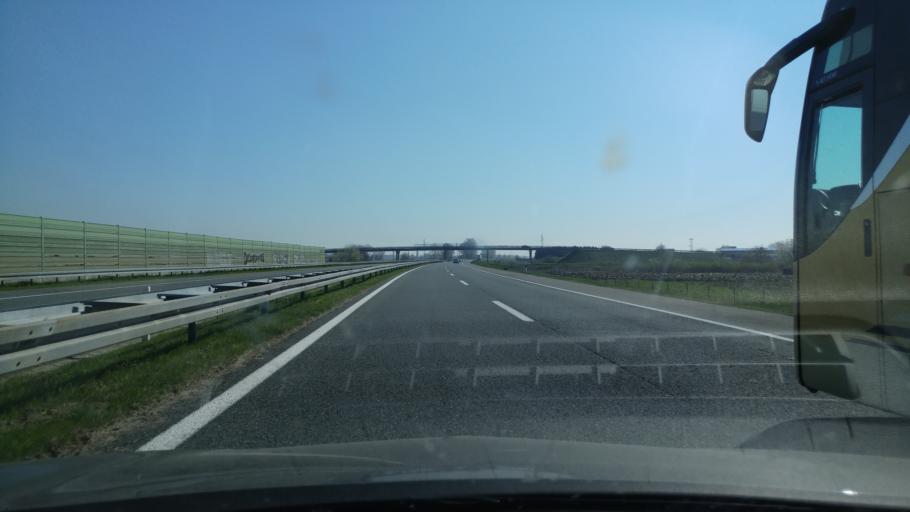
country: HR
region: Brodsko-Posavska
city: Podvinje
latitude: 45.1845
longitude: 18.0282
